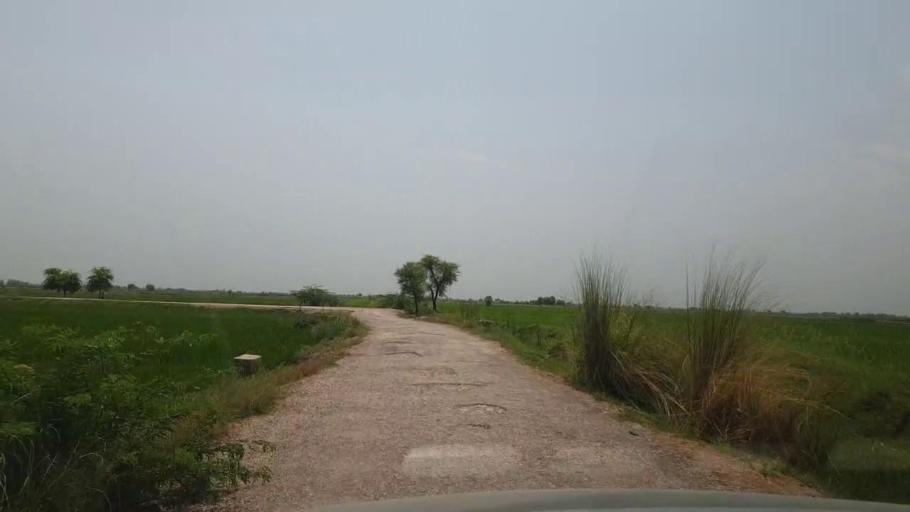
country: PK
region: Sindh
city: Garhi Yasin
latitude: 27.8702
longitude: 68.5013
